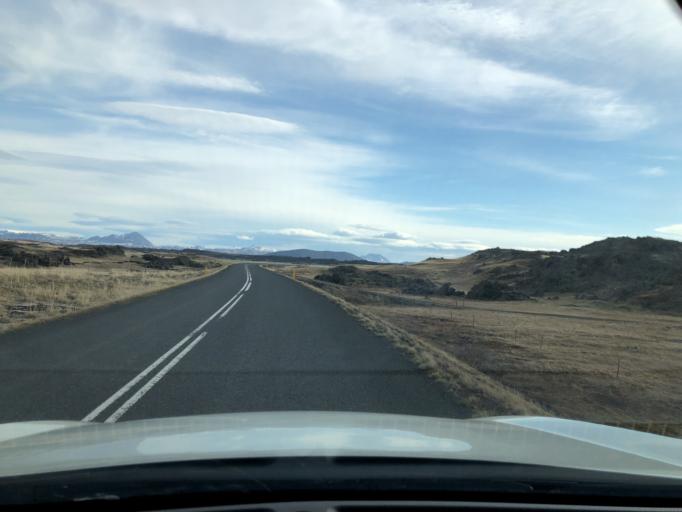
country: IS
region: Northeast
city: Laugar
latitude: 65.5533
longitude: -16.9663
